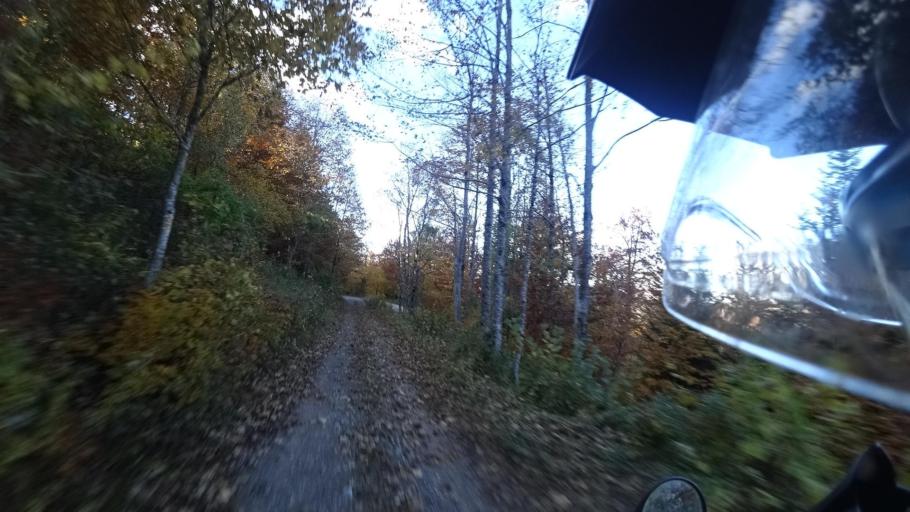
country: HR
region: Karlovacka
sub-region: Grad Ogulin
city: Ogulin
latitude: 45.1873
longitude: 15.1106
